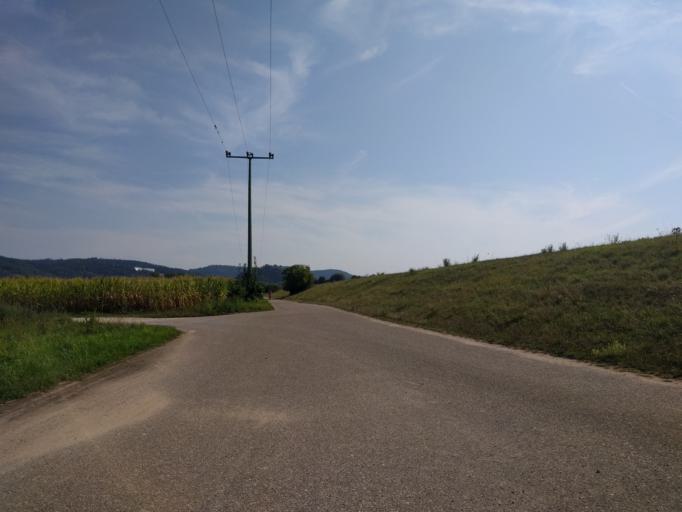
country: DE
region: Bavaria
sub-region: Upper Palatinate
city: Tegernheim
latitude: 49.0220
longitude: 12.1861
